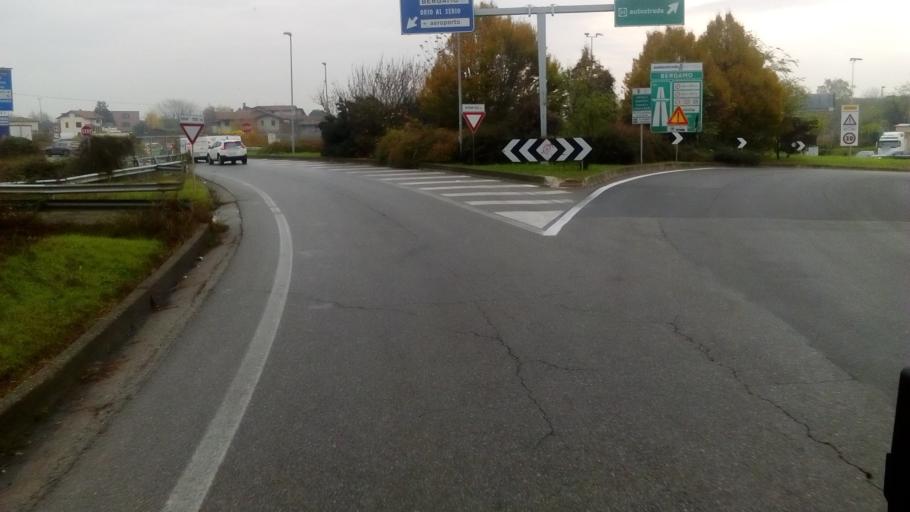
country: IT
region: Lombardy
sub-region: Provincia di Bergamo
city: Azzano San Paolo
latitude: 45.6758
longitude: 9.6687
